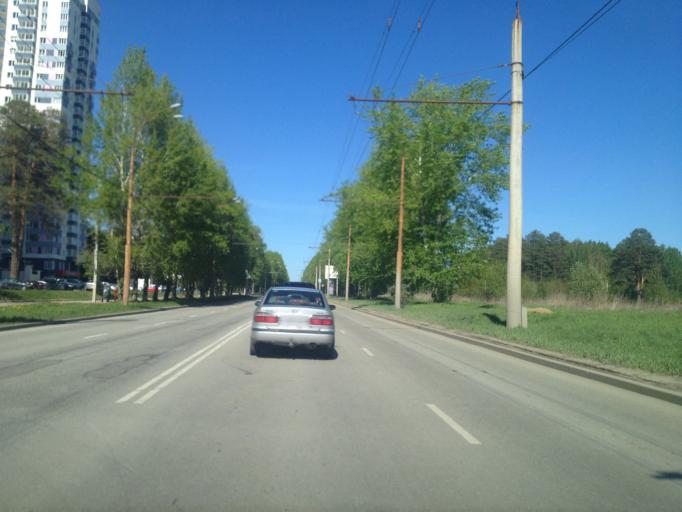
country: RU
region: Sverdlovsk
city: Sovkhoznyy
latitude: 56.7717
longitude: 60.5438
